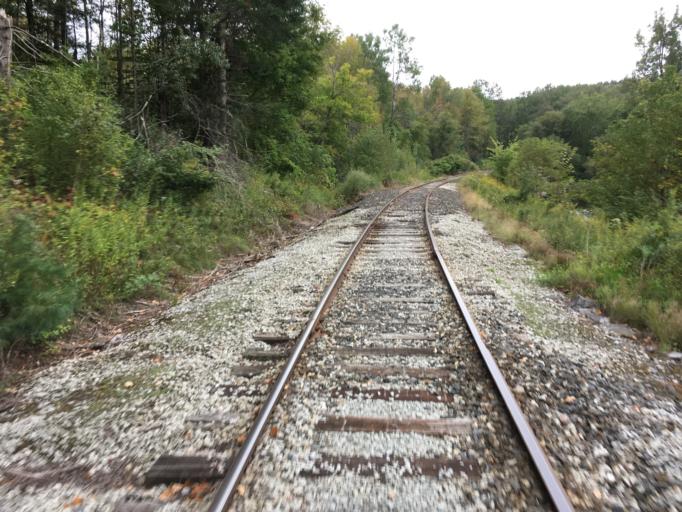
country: US
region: Vermont
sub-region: Washington County
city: Montpelier
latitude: 44.2295
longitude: -72.5495
